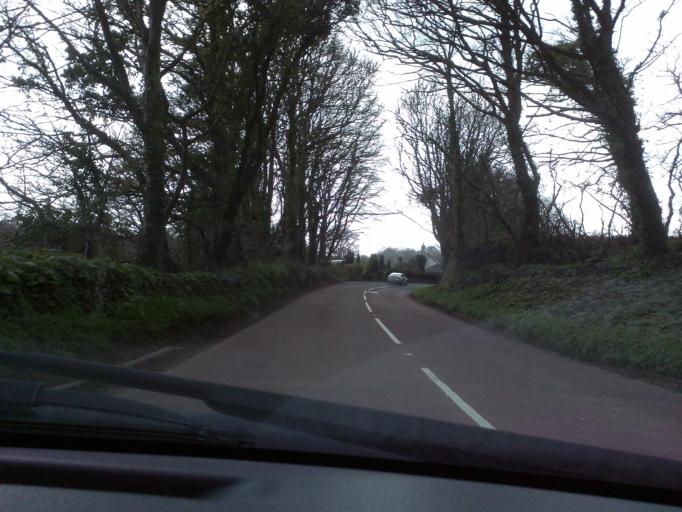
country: GB
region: England
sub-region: Cornwall
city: Penzance
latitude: 50.1099
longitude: -5.5639
